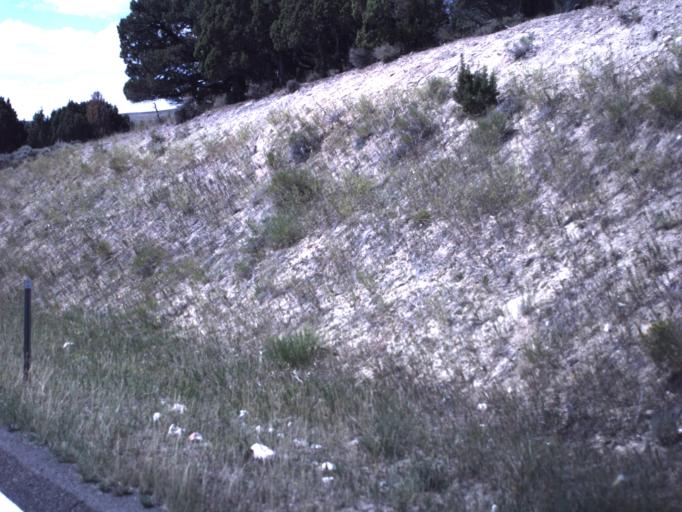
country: US
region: Utah
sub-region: Daggett County
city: Manila
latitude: 40.9851
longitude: -109.8423
